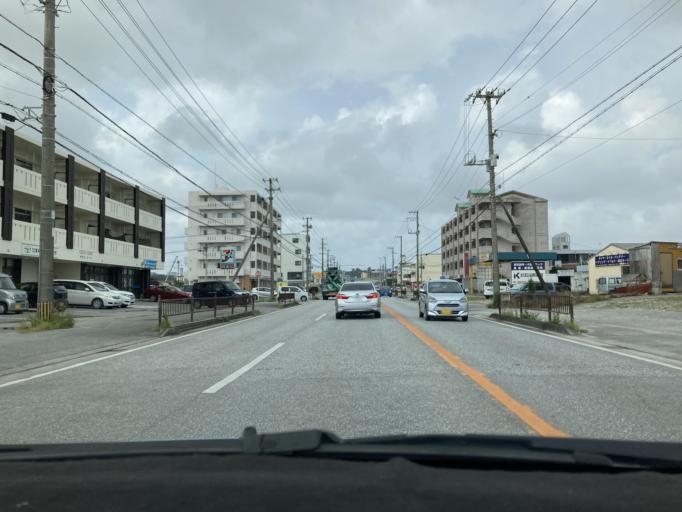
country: JP
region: Okinawa
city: Tomigusuku
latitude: 26.1694
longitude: 127.6673
